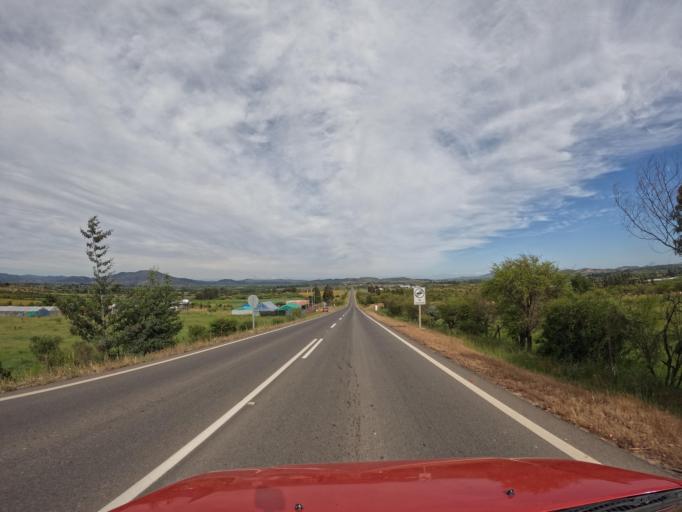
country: CL
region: Maule
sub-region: Provincia de Talca
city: Talca
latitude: -35.3704
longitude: -71.8449
